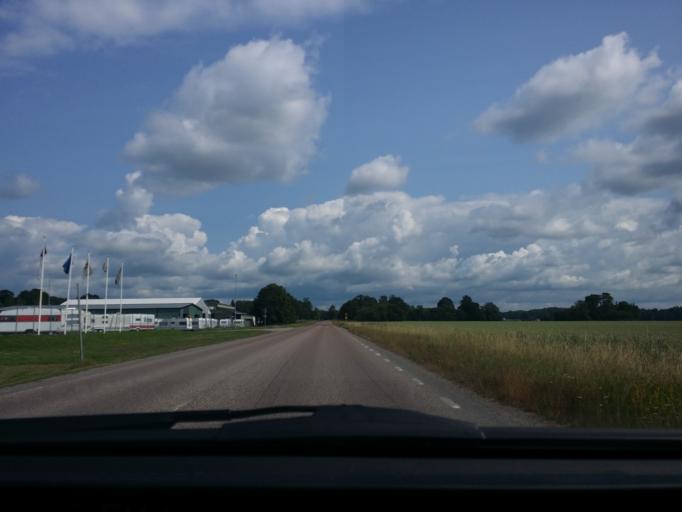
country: SE
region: Vaestmanland
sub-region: Vasteras
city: Hokasen
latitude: 59.6136
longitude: 16.6152
